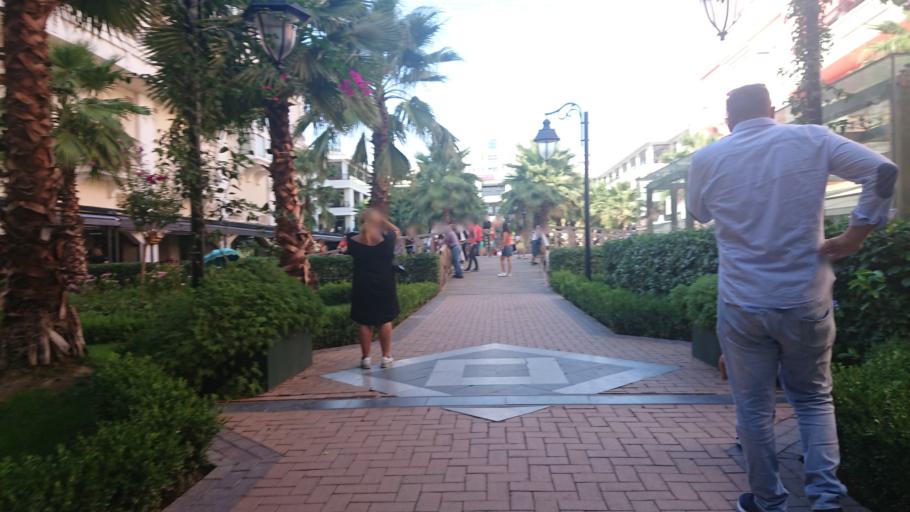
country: TR
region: Izmir
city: Karsiyaka
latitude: 38.4729
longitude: 27.0749
